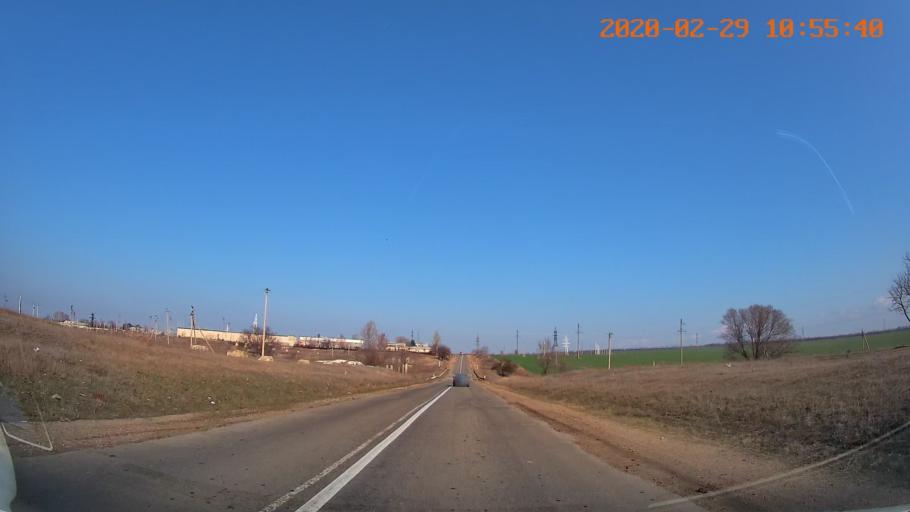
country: MD
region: Telenesti
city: Grigoriopol
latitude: 47.1364
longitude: 29.3253
